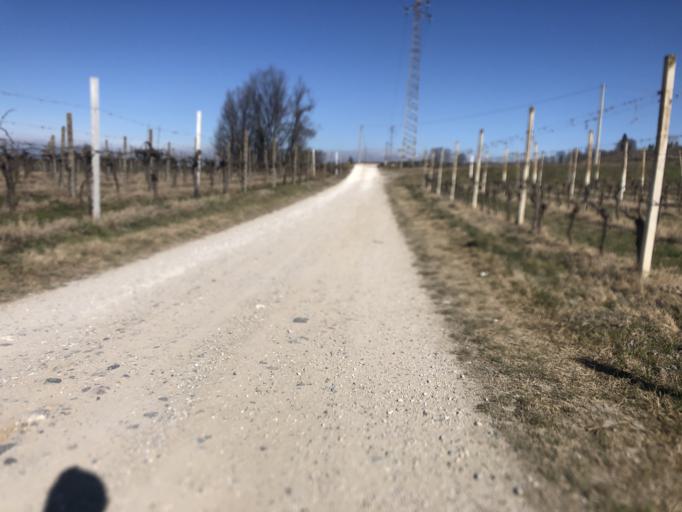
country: IT
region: Veneto
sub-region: Provincia di Verona
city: San Giorgio in Salici
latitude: 45.4234
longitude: 10.8085
